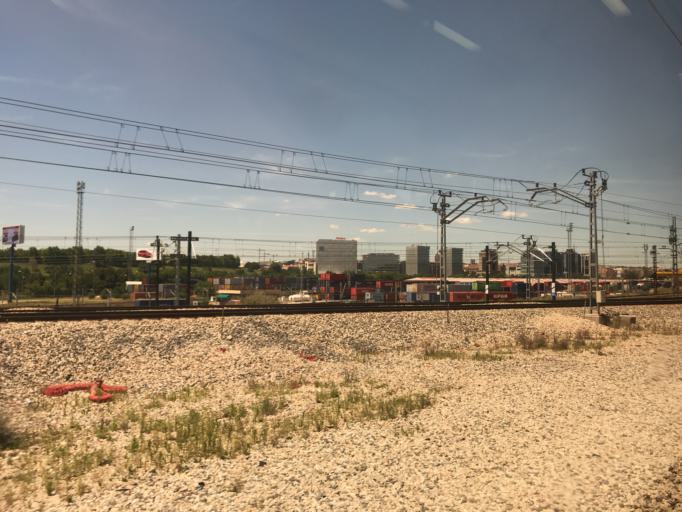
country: ES
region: Madrid
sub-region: Provincia de Madrid
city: Puente de Vallecas
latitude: 40.3837
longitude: -3.6796
